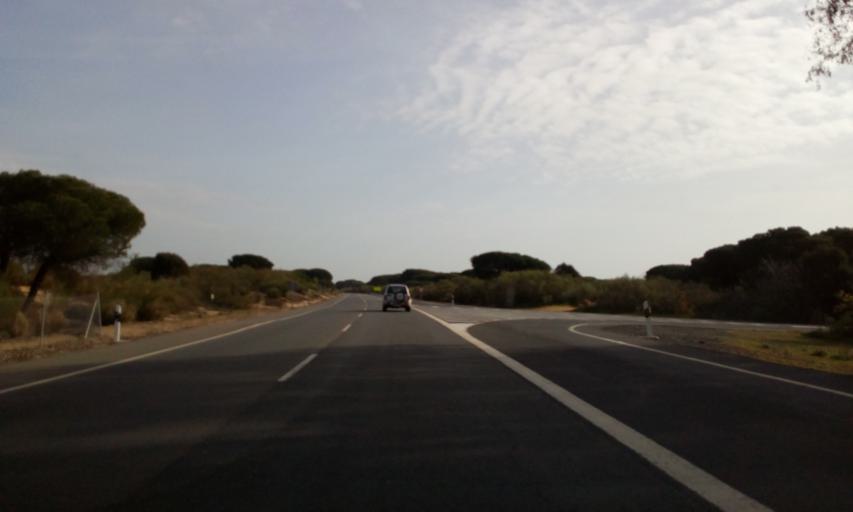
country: ES
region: Andalusia
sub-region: Provincia de Huelva
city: Palos de la Frontera
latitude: 37.1544
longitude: -6.8720
